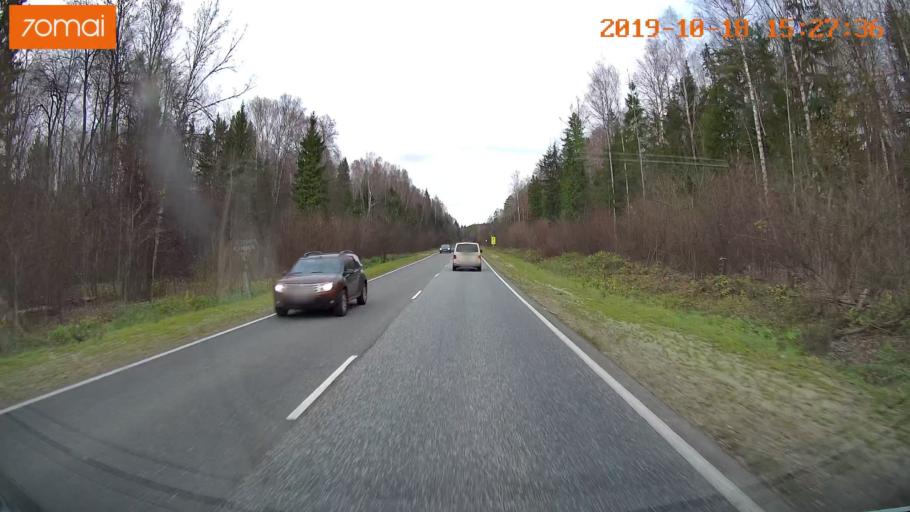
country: RU
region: Vladimir
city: Anopino
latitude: 55.7553
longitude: 40.6716
